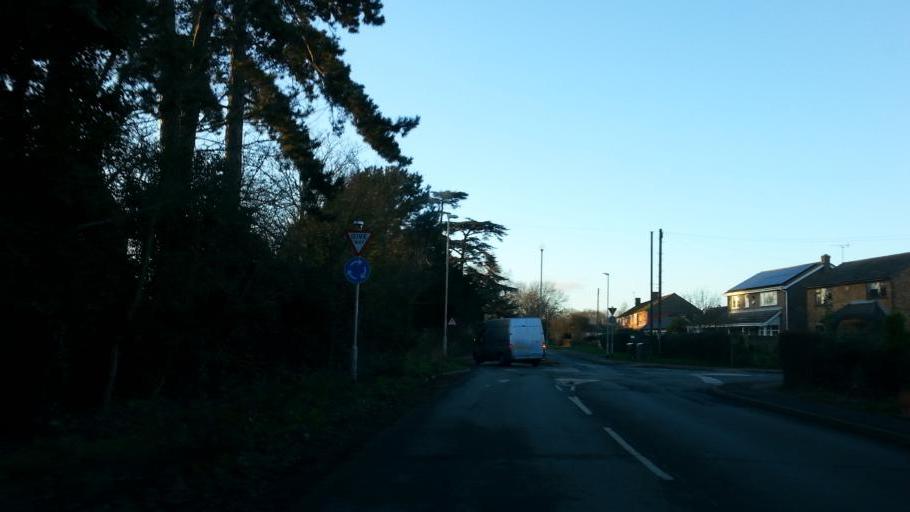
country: GB
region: England
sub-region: Cambridgeshire
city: Hemingford Grey
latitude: 52.2964
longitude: -0.0654
